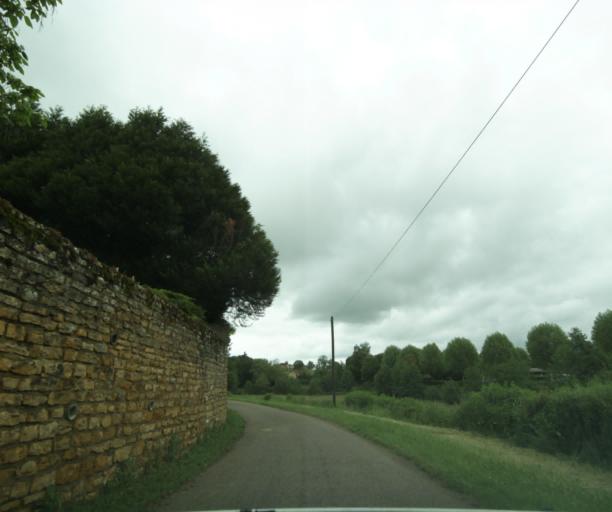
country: FR
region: Bourgogne
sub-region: Departement de Saone-et-Loire
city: Charolles
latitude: 46.4391
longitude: 4.2789
